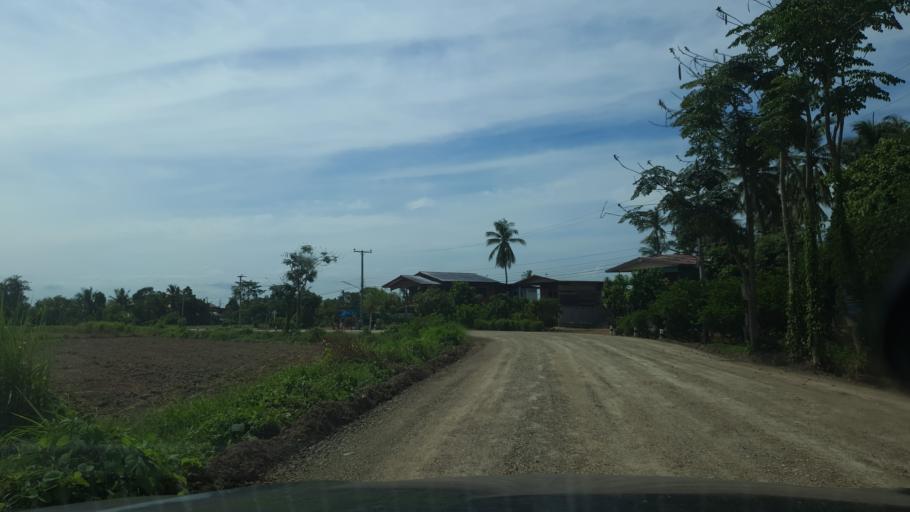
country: TH
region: Sukhothai
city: Si Samrong
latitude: 17.2082
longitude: 99.7195
